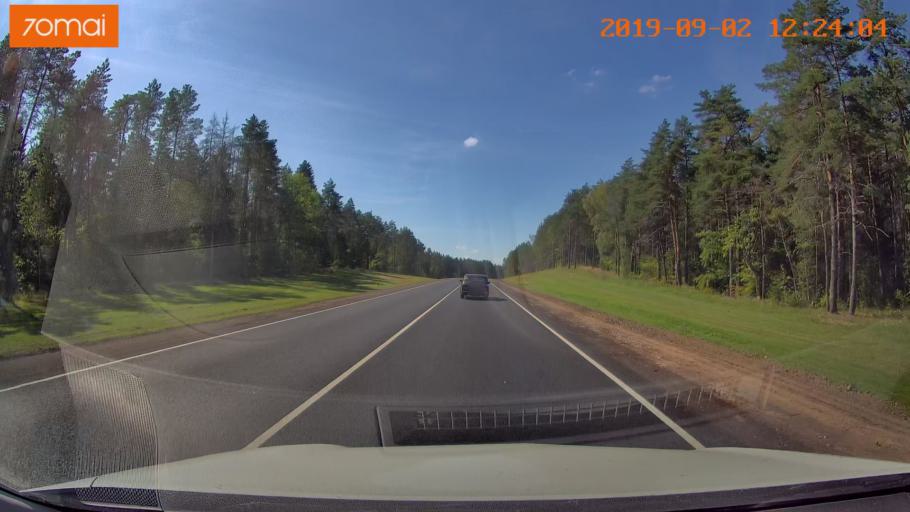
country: RU
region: Smolensk
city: Shumyachi
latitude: 53.8713
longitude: 32.6143
